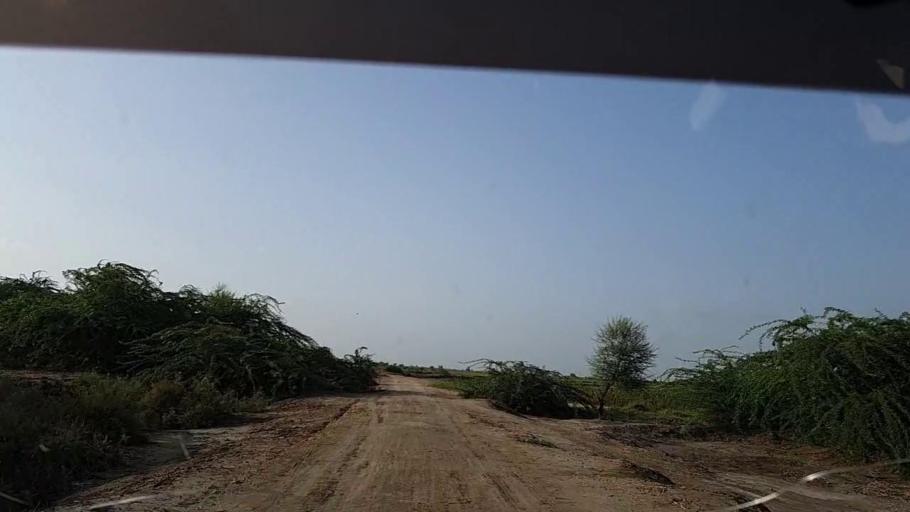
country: PK
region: Sindh
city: Badin
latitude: 24.5687
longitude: 68.8793
